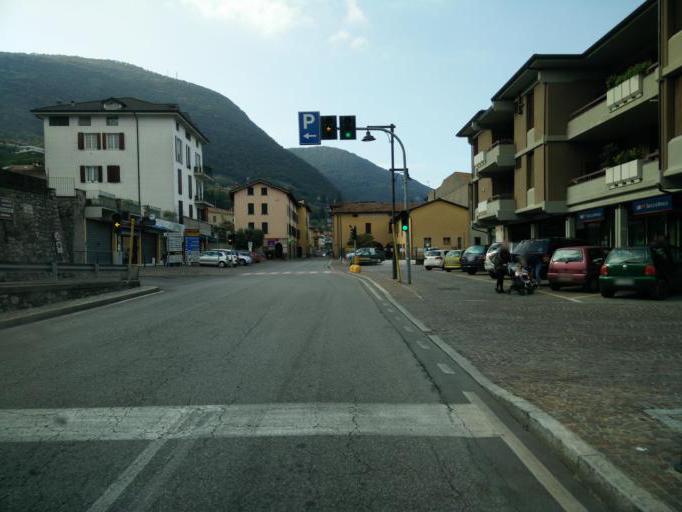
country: IT
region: Lombardy
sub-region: Provincia di Brescia
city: Sulzano
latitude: 45.6899
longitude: 10.1001
